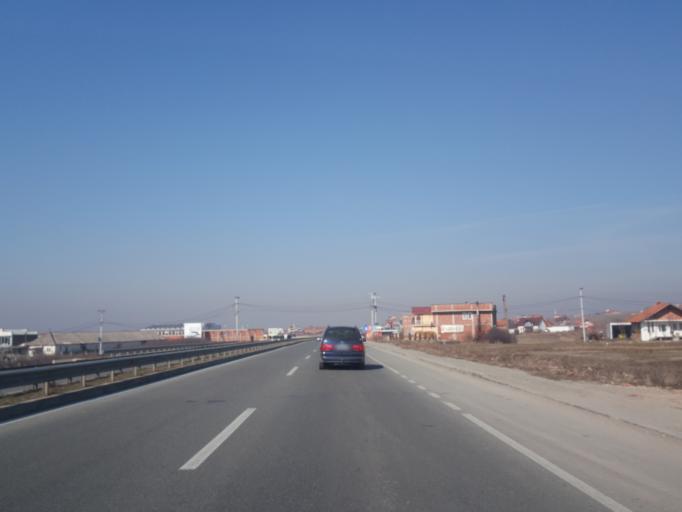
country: XK
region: Pristina
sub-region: Komuna e Obiliqit
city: Obiliq
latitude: 42.7490
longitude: 21.0436
